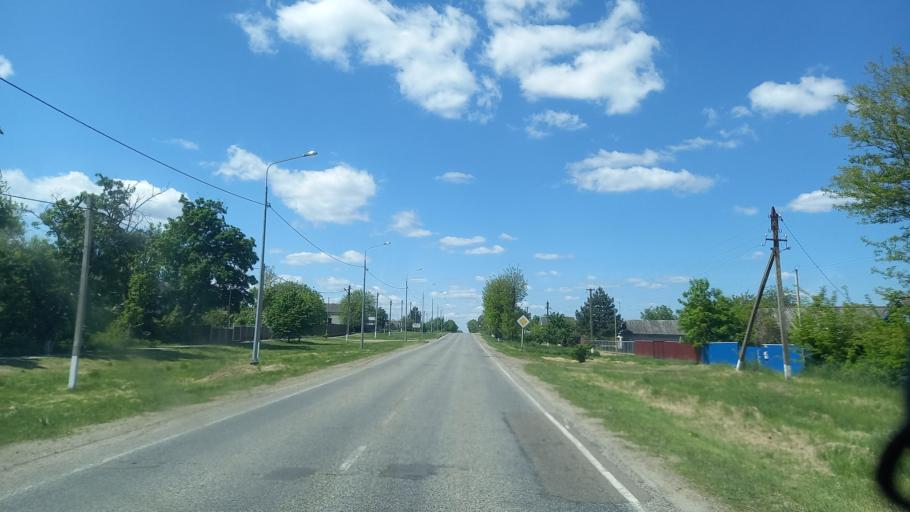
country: RU
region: Krasnodarskiy
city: Tbilisskaya
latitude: 45.3301
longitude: 40.2919
